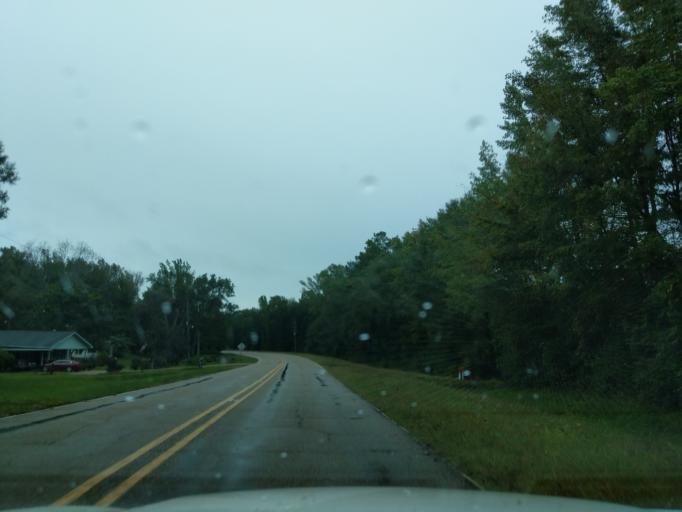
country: US
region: Louisiana
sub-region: Bienville Parish
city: Arcadia
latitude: 32.5509
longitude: -93.0529
